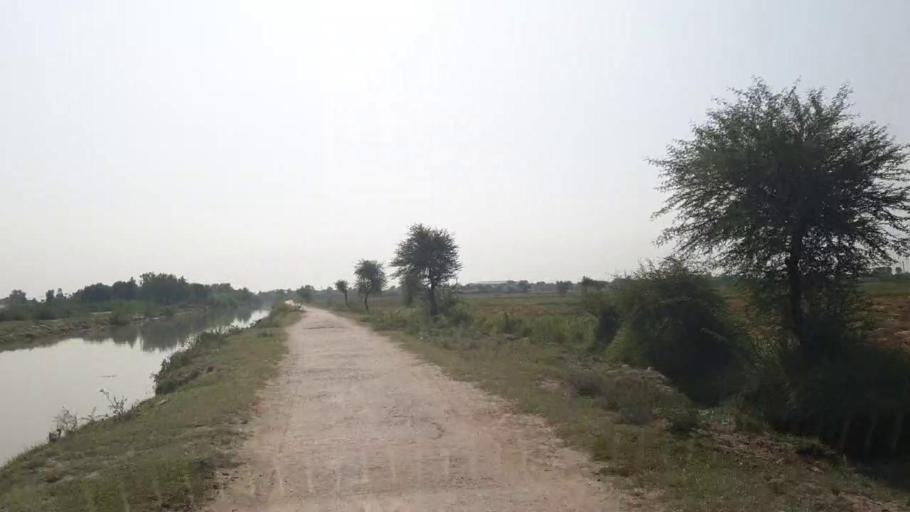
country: PK
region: Sindh
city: Badin
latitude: 24.6441
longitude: 68.8478
